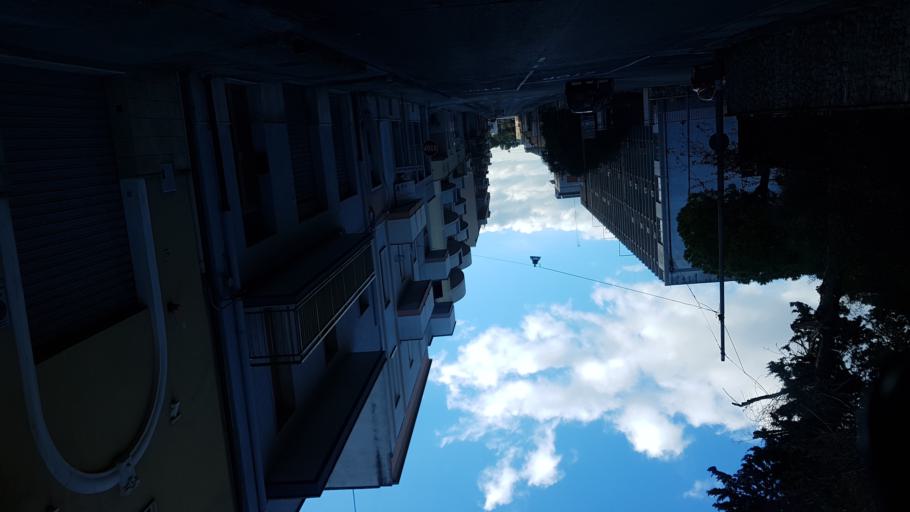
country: IT
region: Apulia
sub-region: Provincia di Brindisi
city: Brindisi
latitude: 40.6318
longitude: 17.9431
